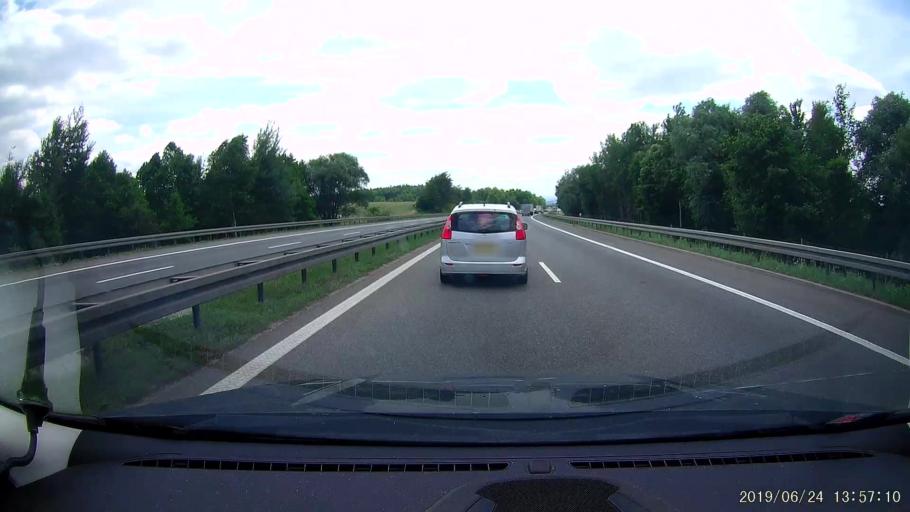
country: PL
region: Lesser Poland Voivodeship
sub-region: Powiat krakowski
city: Kryspinow
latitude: 50.0544
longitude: 19.8095
